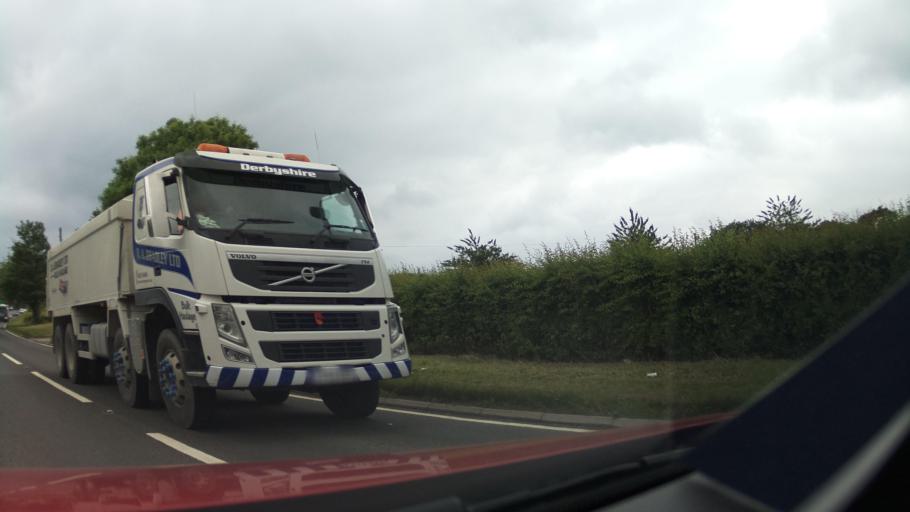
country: GB
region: England
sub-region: Staffordshire
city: Mayfield
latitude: 52.9847
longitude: -1.7469
